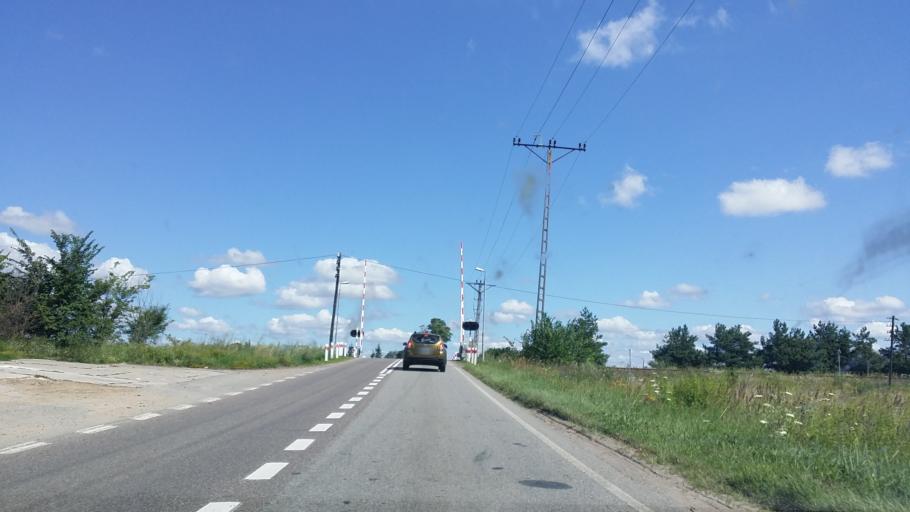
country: PL
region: West Pomeranian Voivodeship
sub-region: Powiat drawski
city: Drawsko Pomorskie
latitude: 53.5176
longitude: 15.7862
